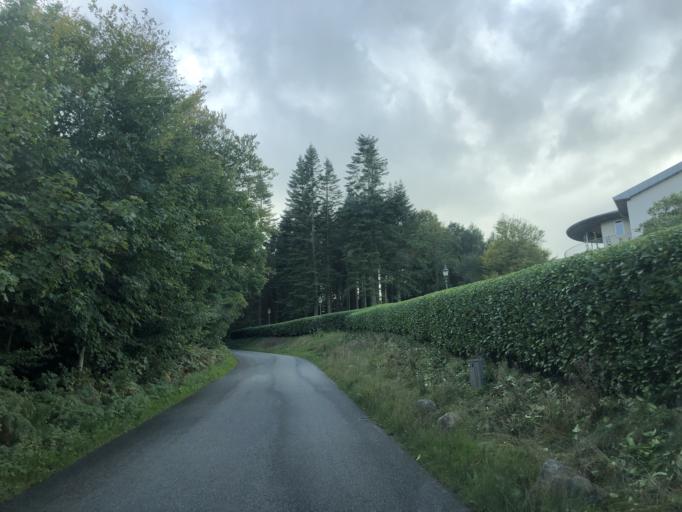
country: DK
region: South Denmark
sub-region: Vejle Kommune
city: Borkop
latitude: 55.6889
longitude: 9.6049
